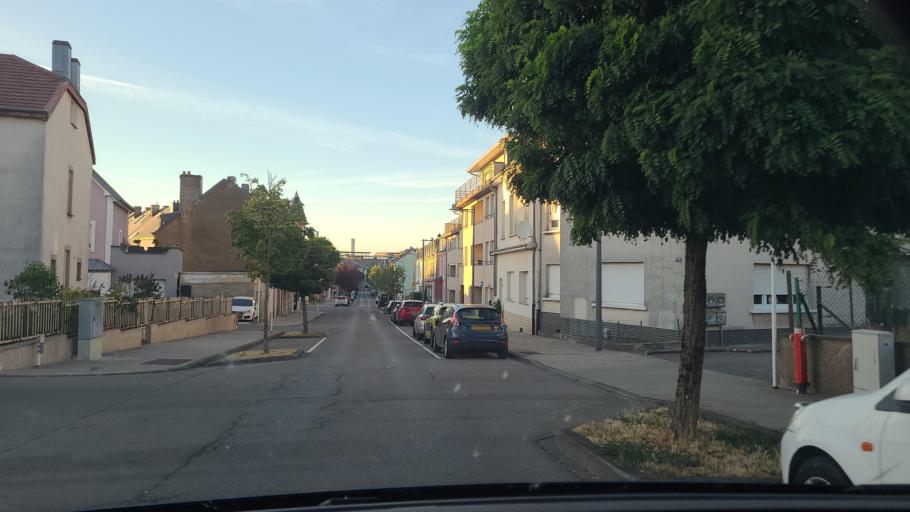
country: LU
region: Luxembourg
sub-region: Canton d'Esch-sur-Alzette
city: Obercorn
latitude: 49.5172
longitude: 5.8975
